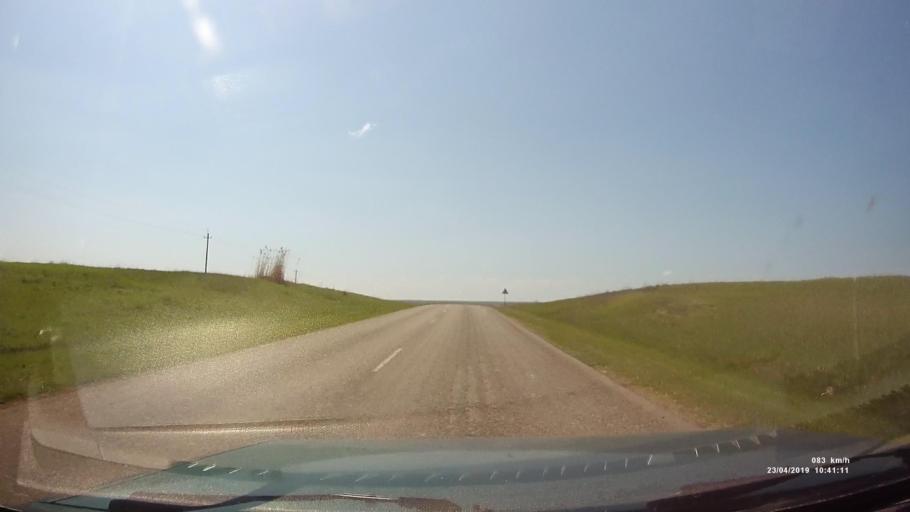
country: RU
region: Kalmykiya
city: Yashalta
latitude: 46.4967
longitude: 42.6382
